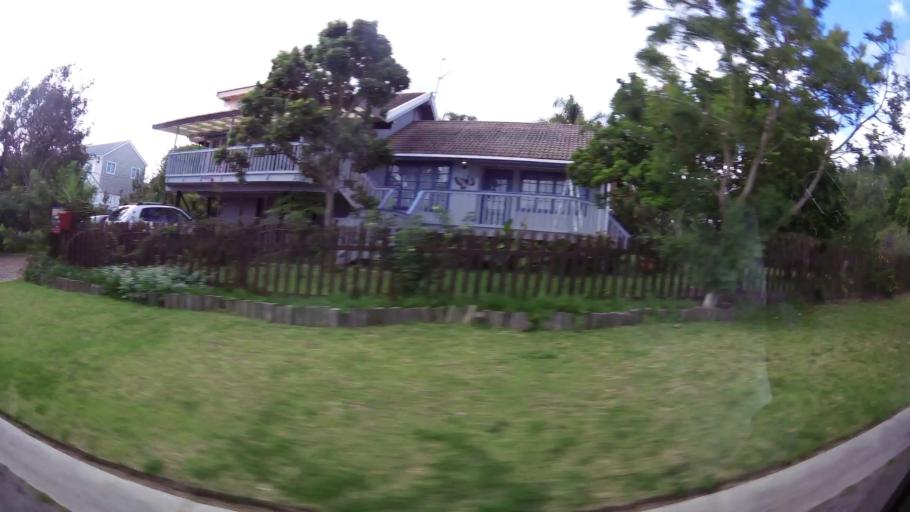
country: ZA
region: Western Cape
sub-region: Eden District Municipality
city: Knysna
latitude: -34.0632
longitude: 23.0784
